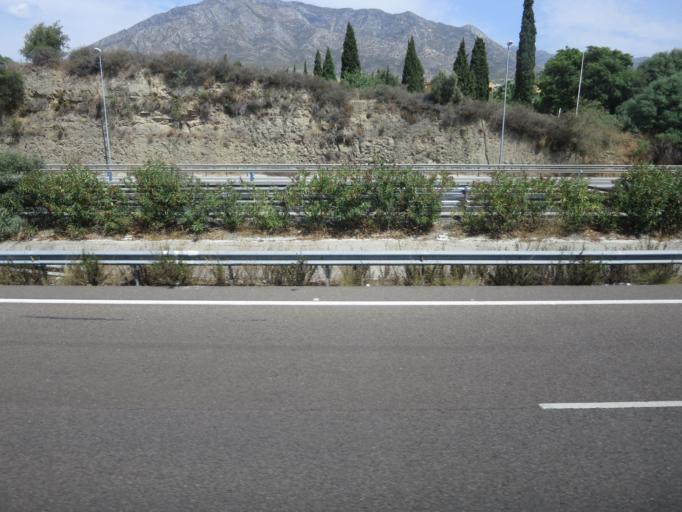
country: ES
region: Andalusia
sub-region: Provincia de Malaga
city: Marbella
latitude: 36.5130
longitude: -4.9306
